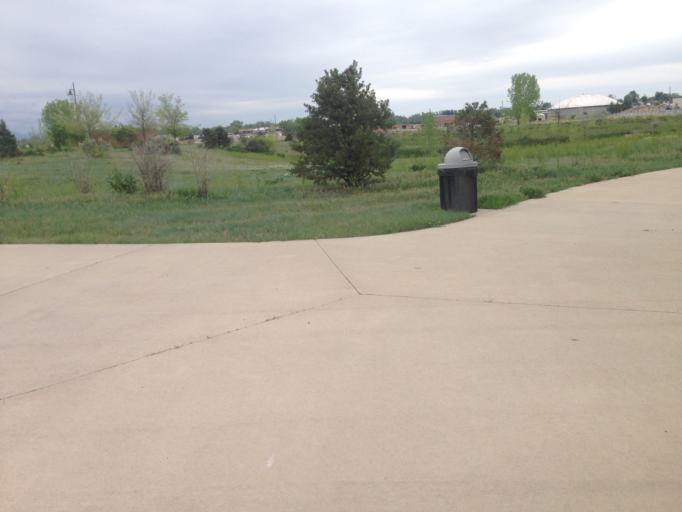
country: US
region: Colorado
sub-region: Boulder County
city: Longmont
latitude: 40.1536
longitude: -105.0897
